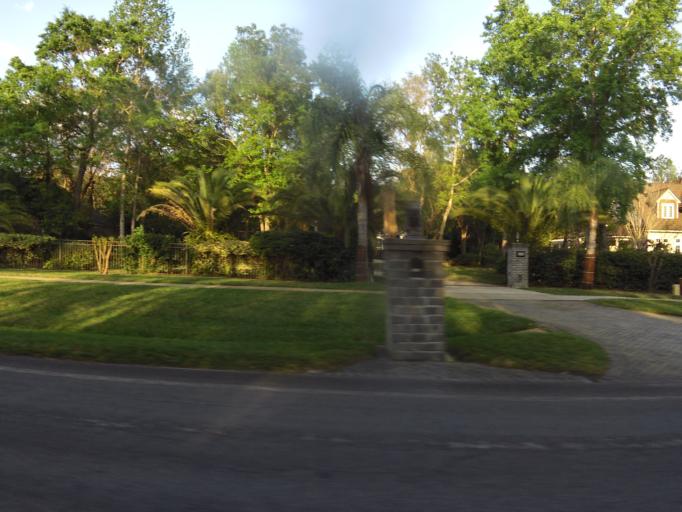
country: US
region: Florida
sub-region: Saint Johns County
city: Fruit Cove
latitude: 30.1186
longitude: -81.5760
